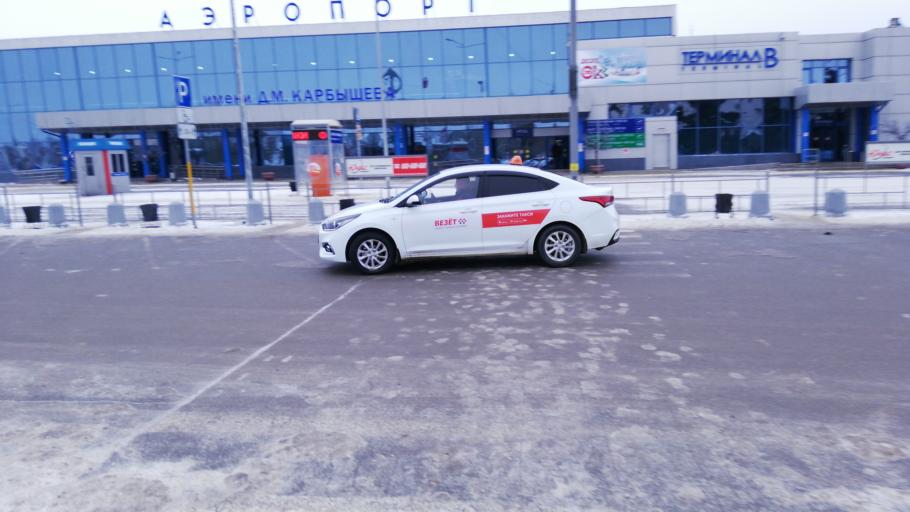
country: RU
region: Omsk
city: Omsk
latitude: 54.9576
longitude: 73.3175
